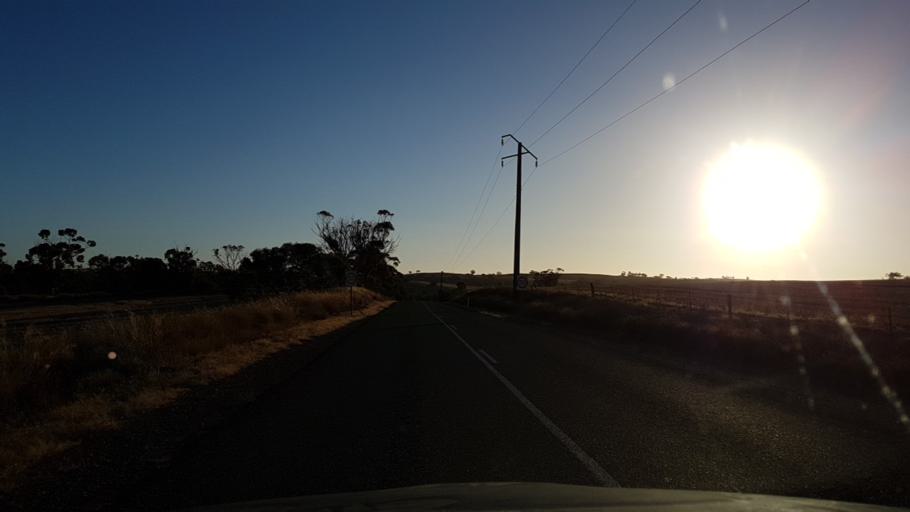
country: AU
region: South Australia
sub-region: Clare and Gilbert Valleys
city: Clare
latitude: -34.0218
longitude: 138.6945
